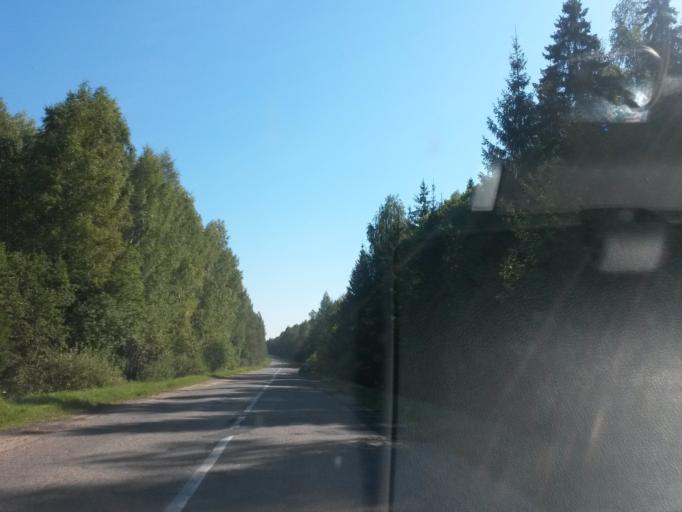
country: RU
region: Jaroslavl
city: Gavrilov-Yam
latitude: 57.2989
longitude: 40.0509
